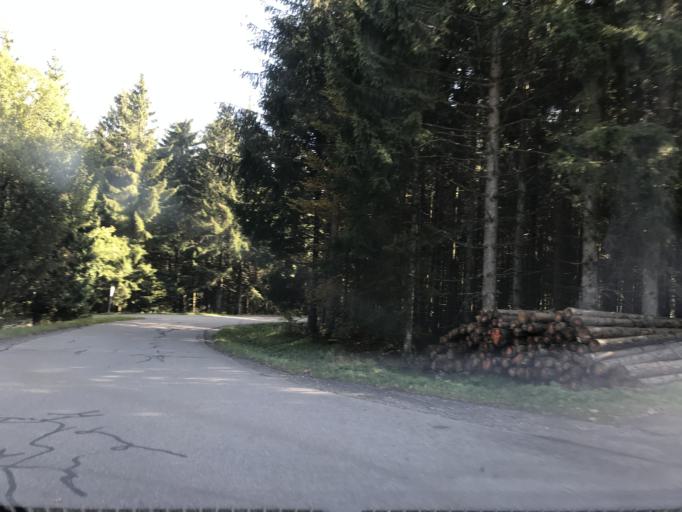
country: DE
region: Baden-Wuerttemberg
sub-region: Freiburg Region
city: Herrischried
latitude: 47.6590
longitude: 7.9661
